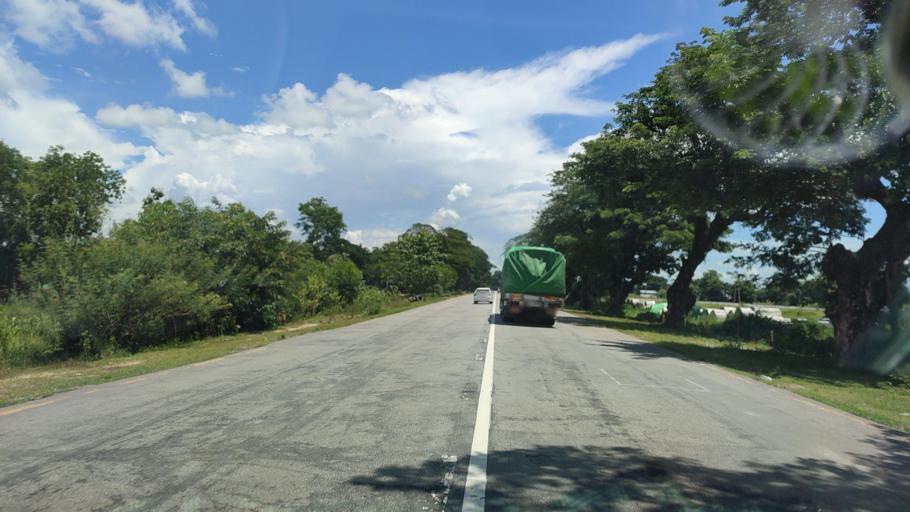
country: MM
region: Bago
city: Nyaunglebin
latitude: 18.1714
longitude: 96.6011
